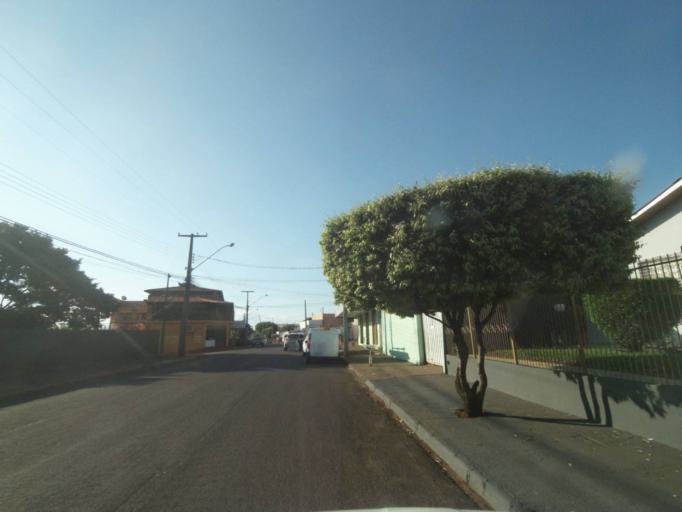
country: BR
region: Parana
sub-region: Cambe
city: Cambe
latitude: -23.3054
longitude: -51.2256
